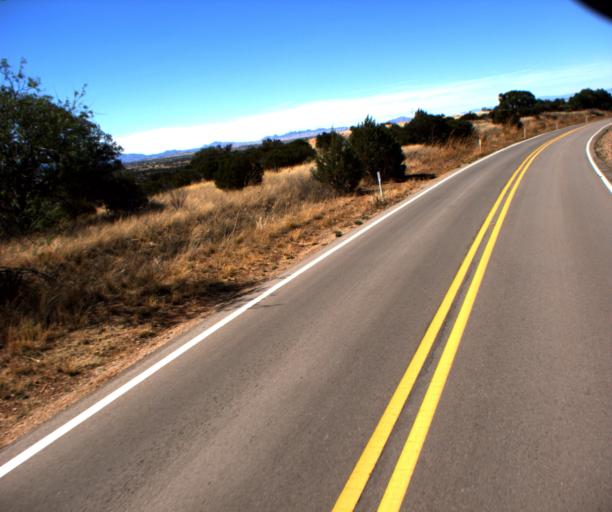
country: US
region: Arizona
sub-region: Cochise County
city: Huachuca City
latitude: 31.5260
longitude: -110.5026
